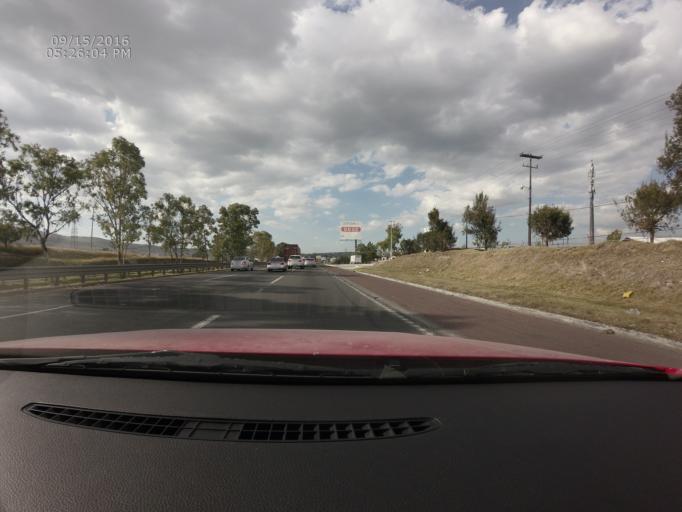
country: MX
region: Mexico
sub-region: Cuautitlan
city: Barrio Tlatenco
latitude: 19.7351
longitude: -99.2107
